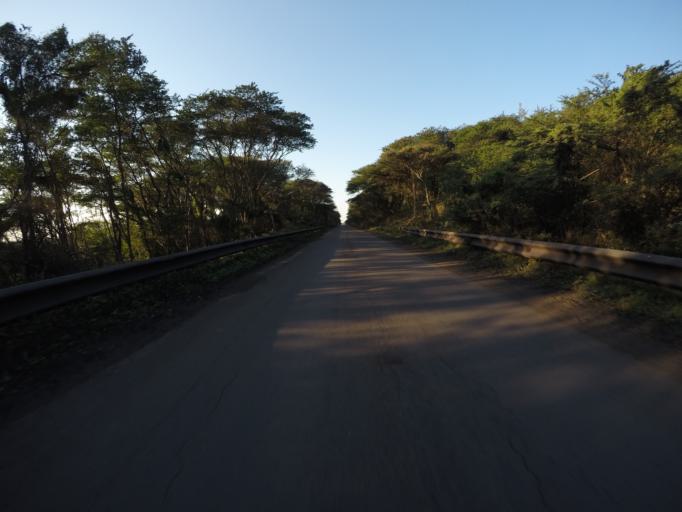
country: ZA
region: KwaZulu-Natal
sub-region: uThungulu District Municipality
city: KwaMbonambi
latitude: -28.6985
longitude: 32.2067
